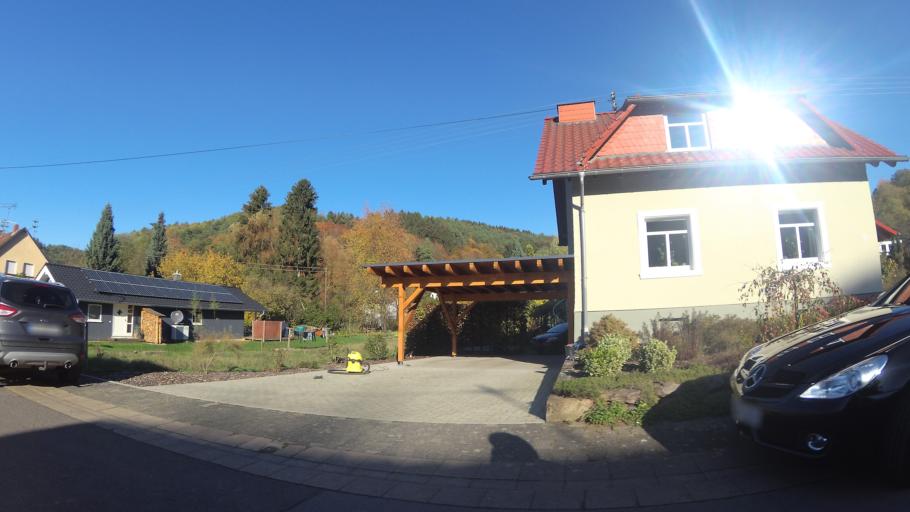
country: DE
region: Saarland
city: Losheim
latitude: 49.4698
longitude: 6.7268
